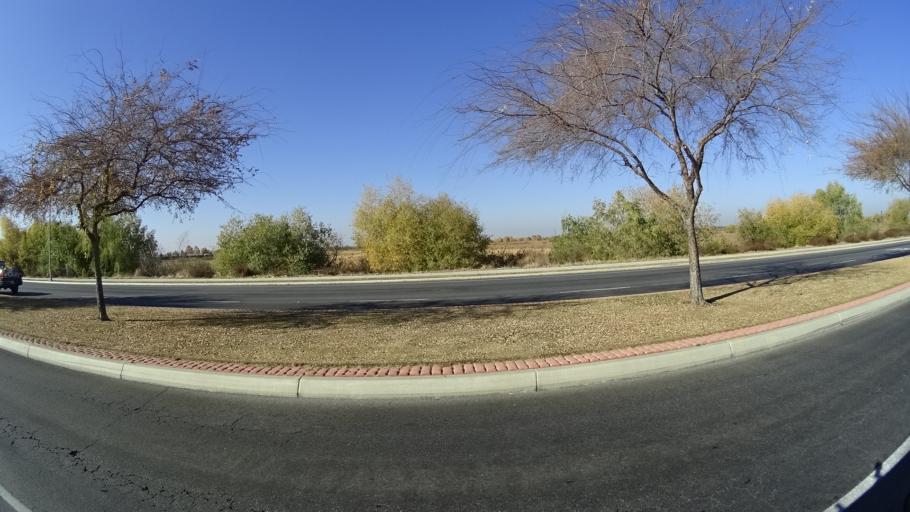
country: US
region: California
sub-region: Kern County
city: Rosedale
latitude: 35.3411
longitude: -119.1454
